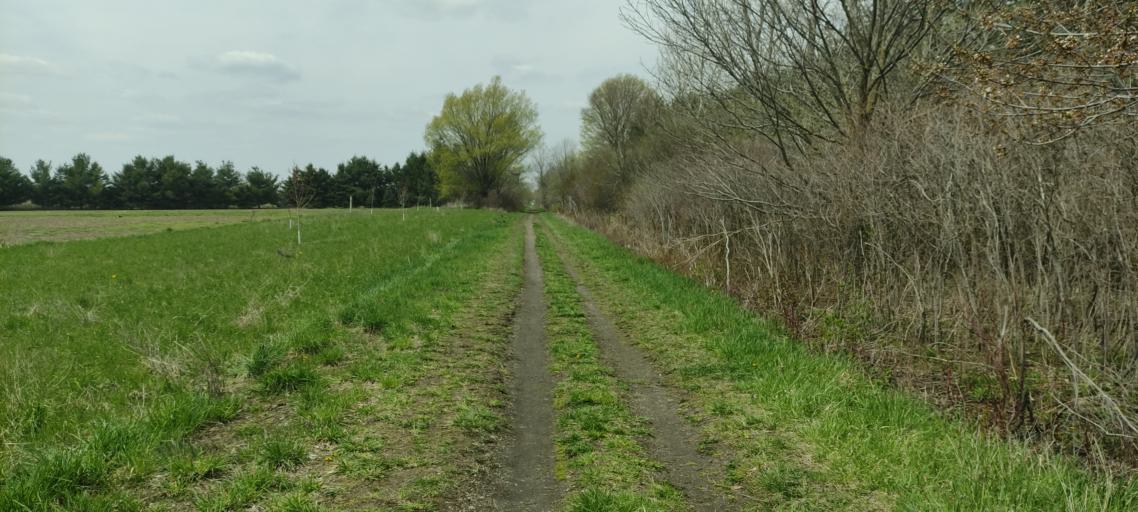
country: CA
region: Ontario
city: Stratford
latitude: 43.3171
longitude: -80.8218
